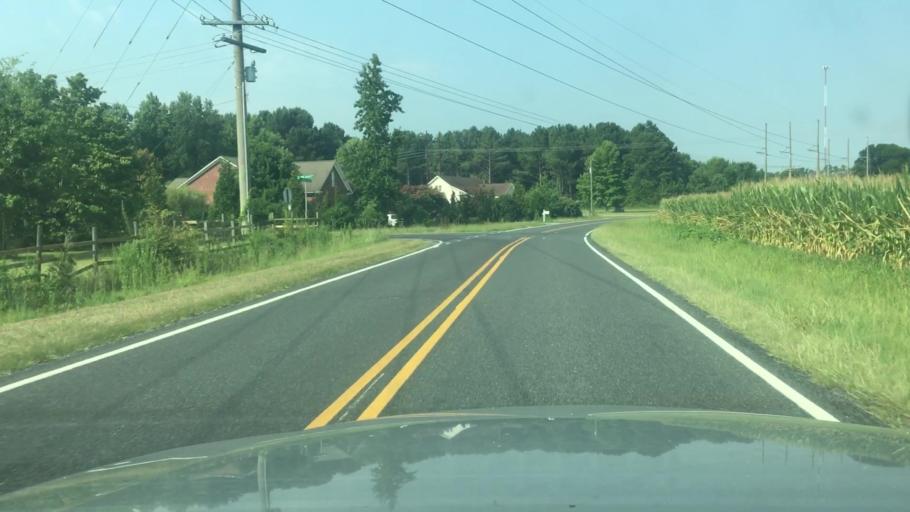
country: US
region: North Carolina
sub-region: Cumberland County
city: Hope Mills
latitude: 34.8989
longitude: -78.8847
